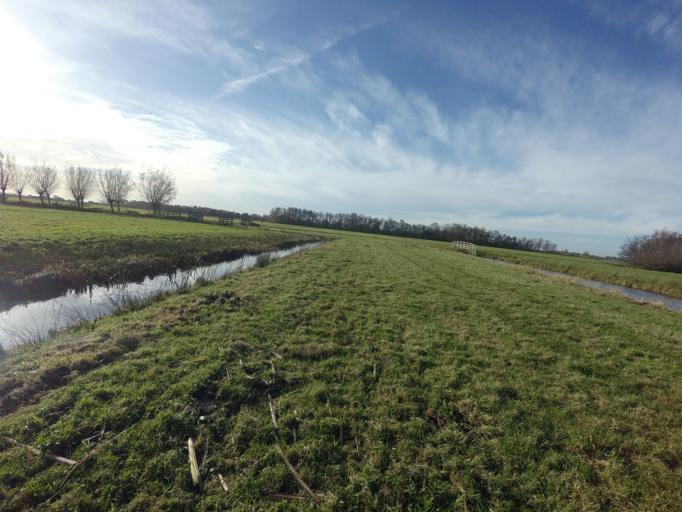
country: NL
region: South Holland
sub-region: Gemeente Vlist
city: Haastrecht
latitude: 52.0294
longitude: 4.7773
